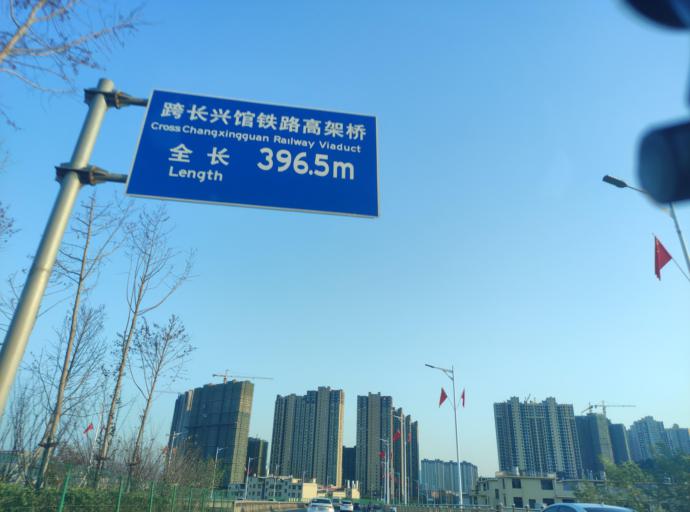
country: CN
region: Jiangxi Sheng
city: Pingxiang
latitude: 27.6402
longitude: 113.8291
